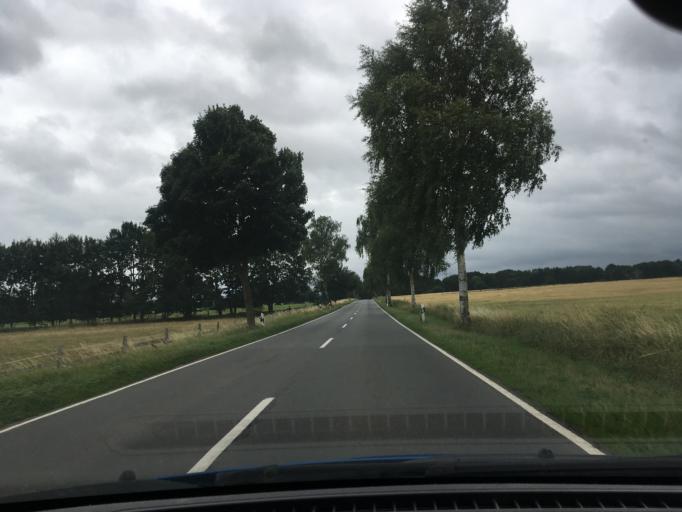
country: DE
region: Lower Saxony
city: Toppenstedt
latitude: 53.2571
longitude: 10.1025
